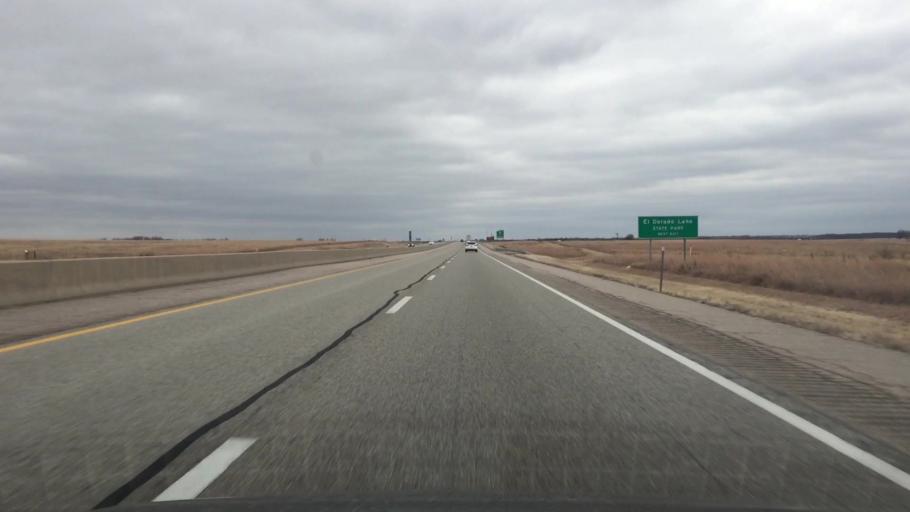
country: US
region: Kansas
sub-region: Butler County
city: El Dorado
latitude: 37.8917
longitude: -96.8372
